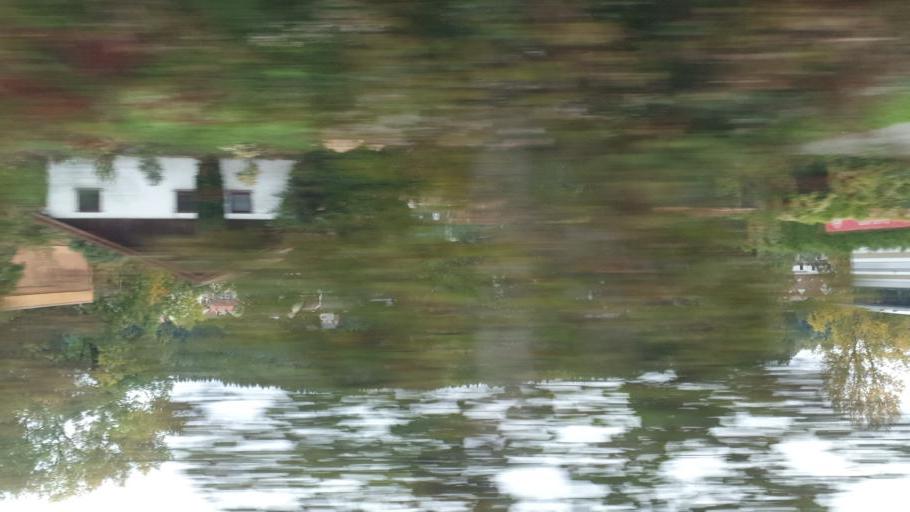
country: DE
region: Saarland
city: Kirkel
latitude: 49.2440
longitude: 7.1982
